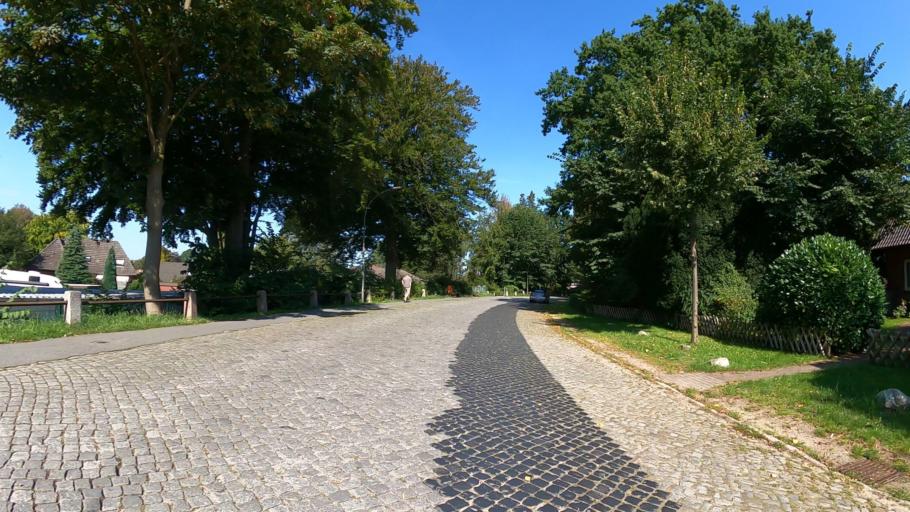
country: DE
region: Schleswig-Holstein
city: Bad Bramstedt
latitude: 53.9146
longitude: 9.8808
